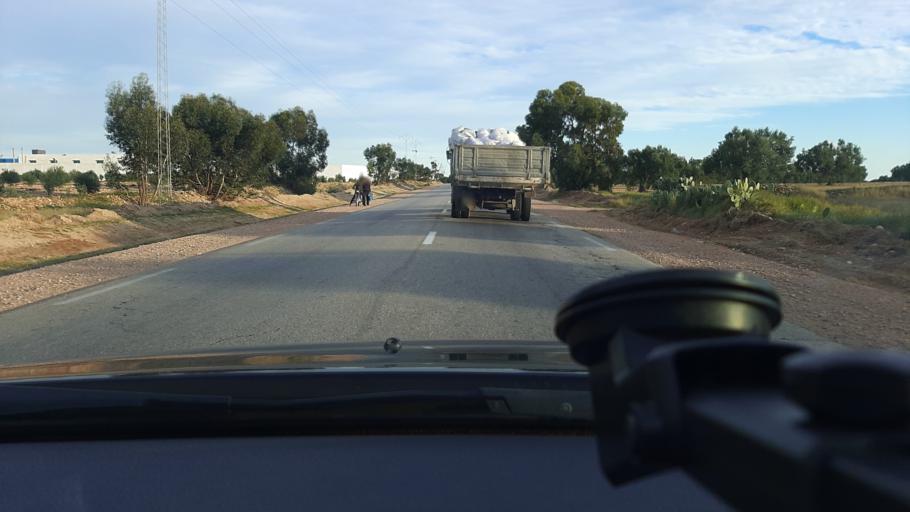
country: TN
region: Al Mahdiyah
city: Shurban
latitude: 34.9272
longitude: 10.4377
